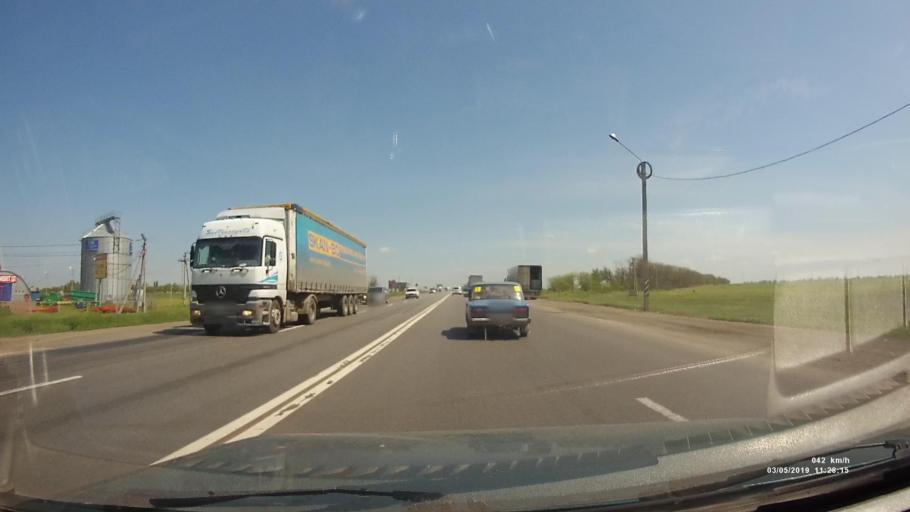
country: RU
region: Rostov
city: Bataysk
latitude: 47.0819
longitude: 39.7752
